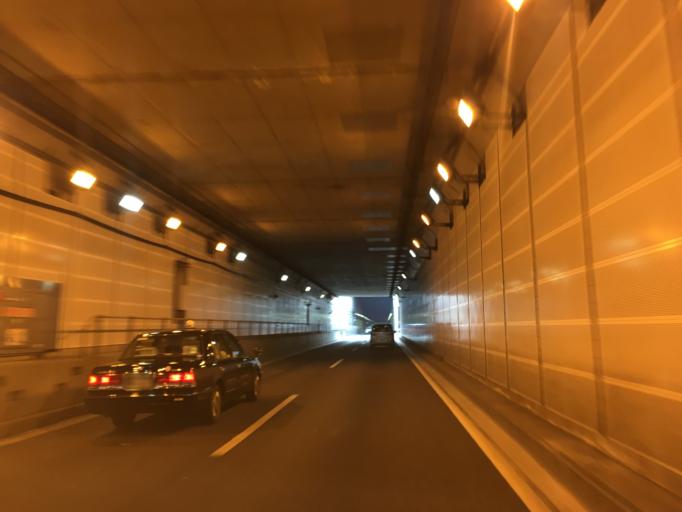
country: JP
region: Saitama
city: Wako
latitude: 35.7312
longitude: 139.6146
